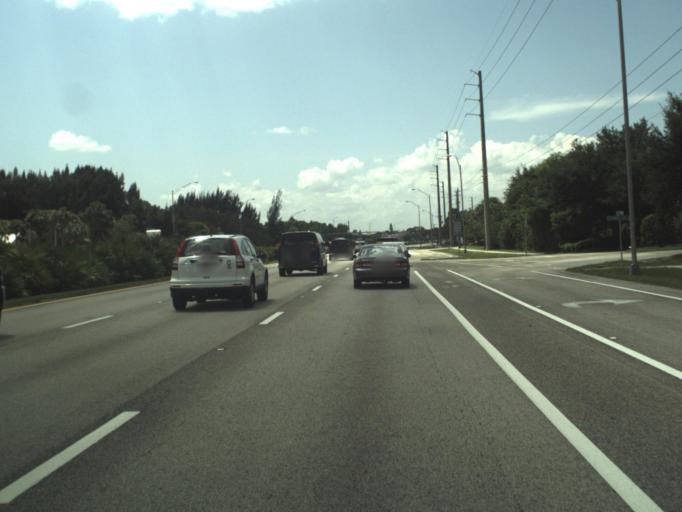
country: US
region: Florida
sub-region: Martin County
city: Port Salerno
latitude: 27.1296
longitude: -80.2005
